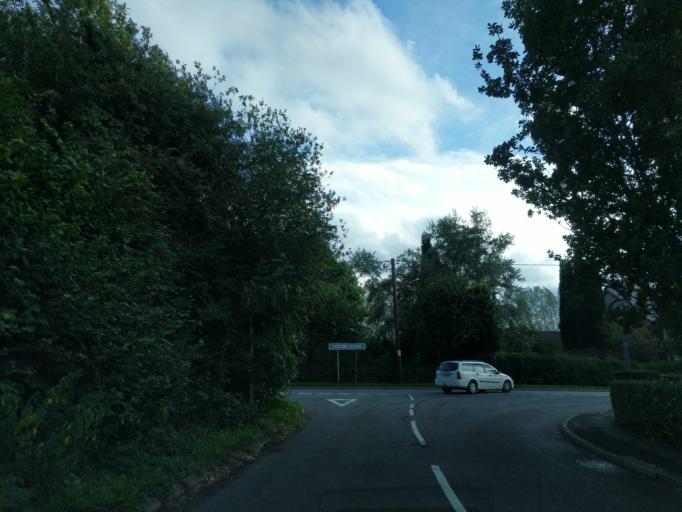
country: GB
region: England
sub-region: Leicestershire
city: Ibstock
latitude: 52.6987
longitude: -1.3869
